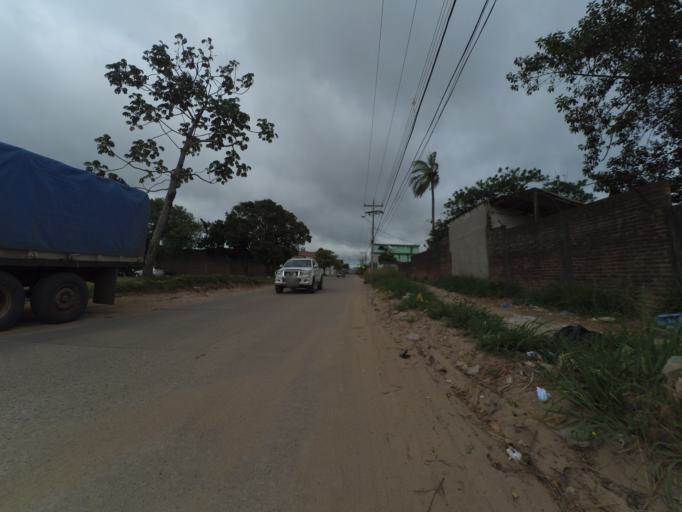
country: BO
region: Santa Cruz
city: Santa Cruz de la Sierra
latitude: -17.8125
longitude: -63.2115
